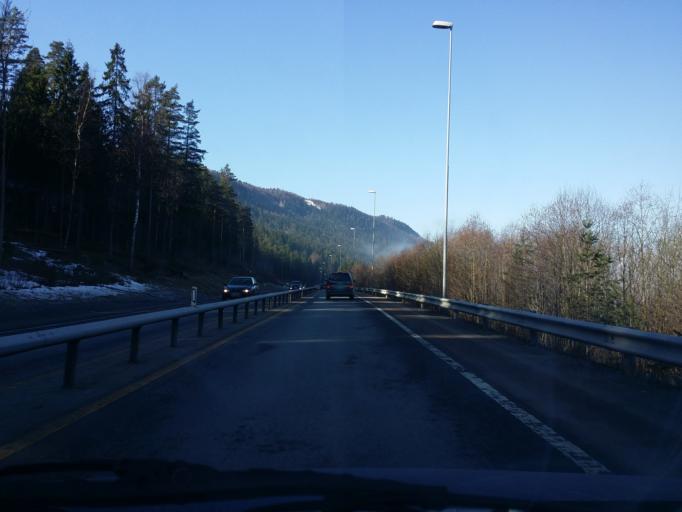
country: NO
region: Buskerud
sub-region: Nedre Eiker
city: Mjondalen
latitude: 59.7429
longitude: 10.0950
